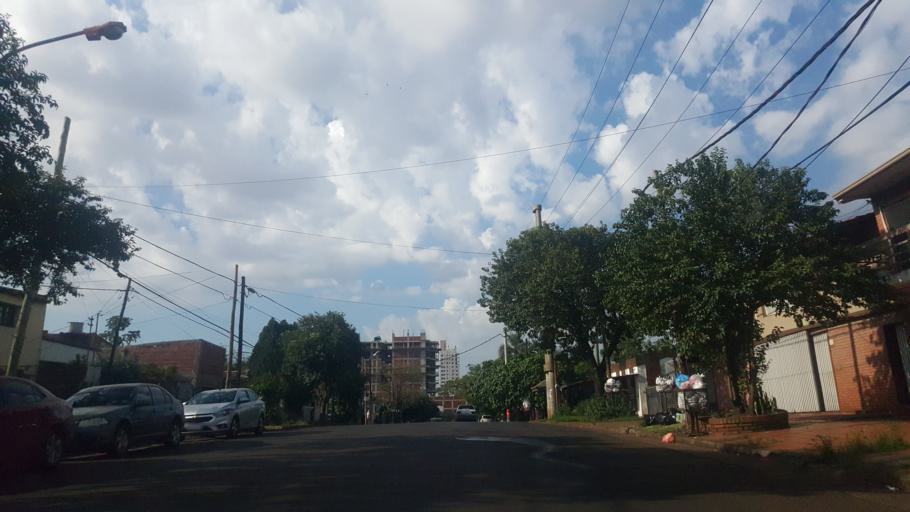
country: AR
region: Misiones
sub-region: Departamento de Capital
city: Posadas
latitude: -27.3770
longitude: -55.8913
